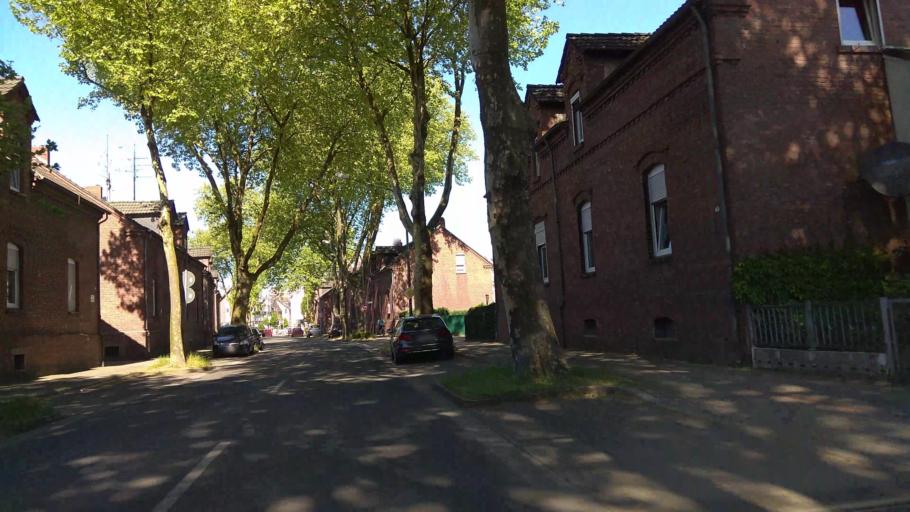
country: DE
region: North Rhine-Westphalia
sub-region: Regierungsbezirk Munster
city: Bottrop
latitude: 51.5468
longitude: 6.9391
